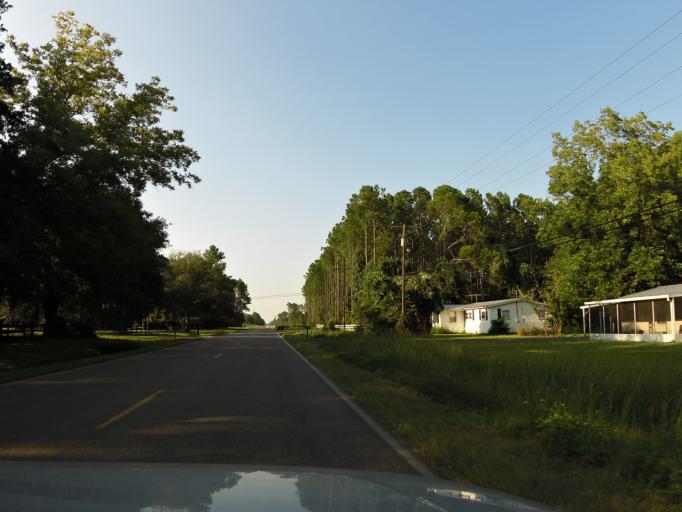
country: US
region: Florida
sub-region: Duval County
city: Baldwin
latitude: 30.3167
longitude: -82.0085
